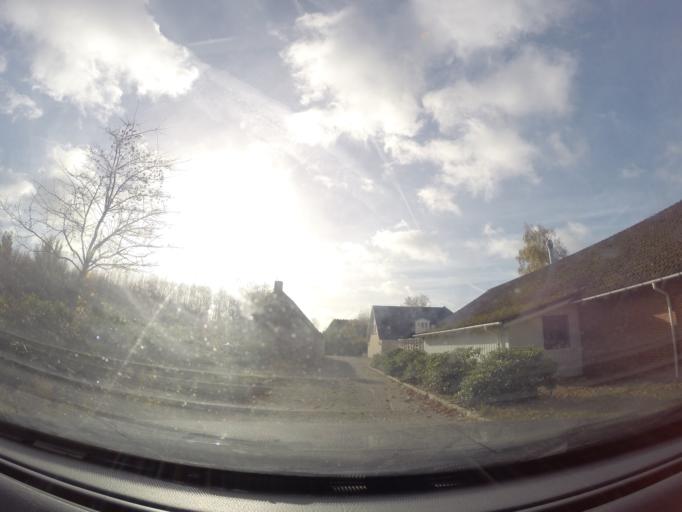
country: DK
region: South Denmark
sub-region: Faaborg-Midtfyn Kommune
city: Ringe
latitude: 55.2154
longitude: 10.5637
